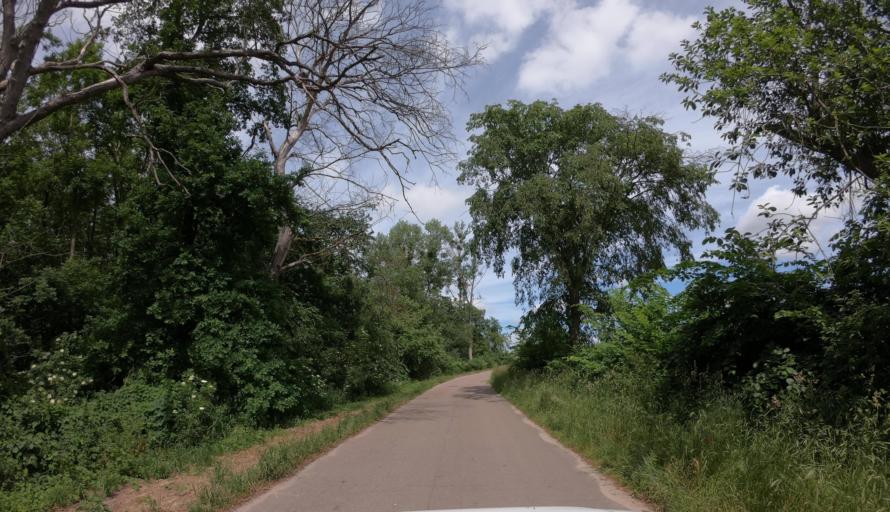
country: PL
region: West Pomeranian Voivodeship
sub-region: Powiat kamienski
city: Wolin
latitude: 53.8283
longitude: 14.7079
